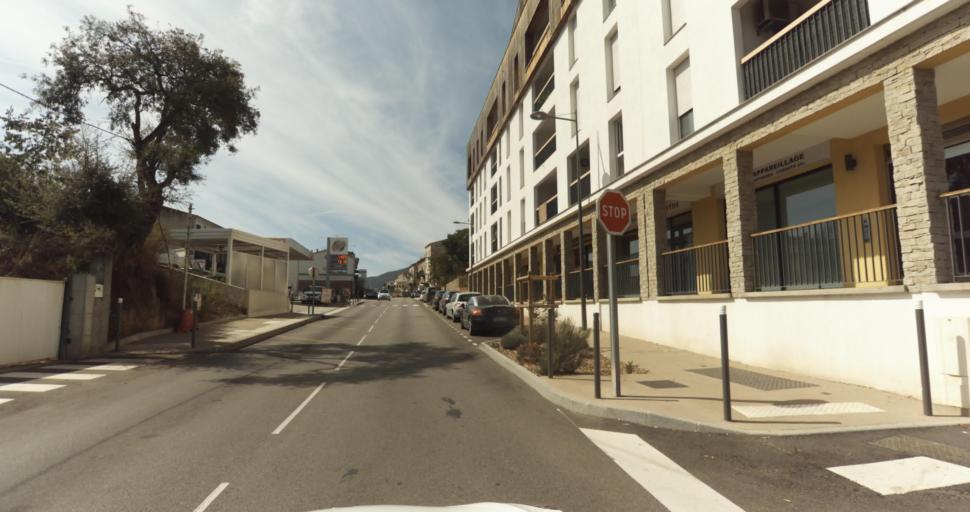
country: FR
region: Corsica
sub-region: Departement de la Corse-du-Sud
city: Afa
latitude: 41.9525
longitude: 8.7820
